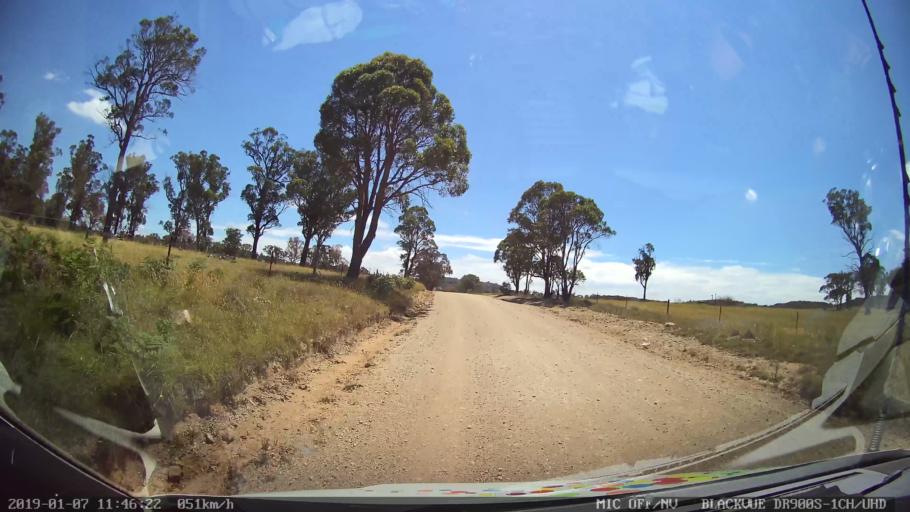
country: AU
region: New South Wales
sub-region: Guyra
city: Guyra
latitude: -30.3427
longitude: 151.6130
